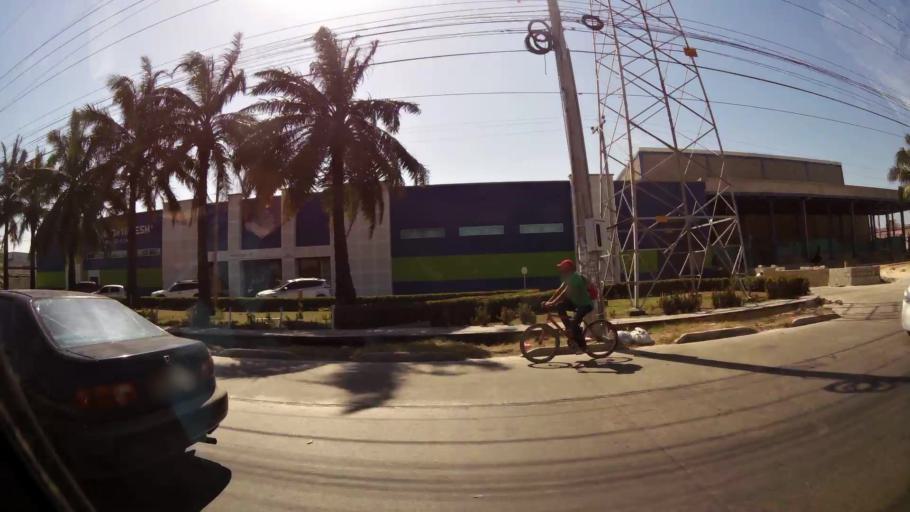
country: CO
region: Atlantico
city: Barranquilla
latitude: 10.9419
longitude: -74.7834
